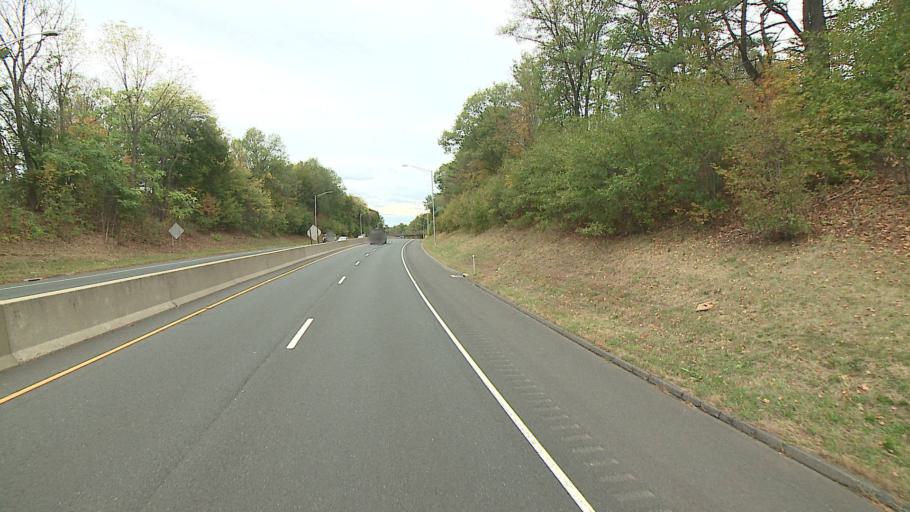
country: US
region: Connecticut
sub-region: Middlesex County
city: Middletown
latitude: 41.5476
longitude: -72.6308
